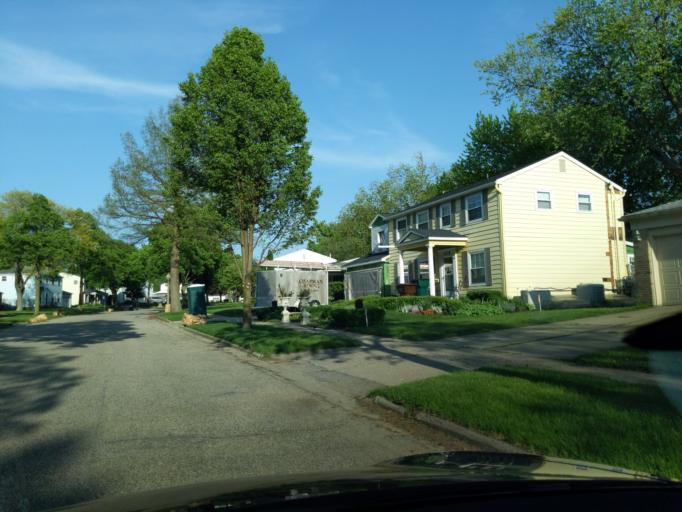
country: US
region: Michigan
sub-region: Ingham County
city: East Lansing
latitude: 42.7532
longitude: -84.5204
